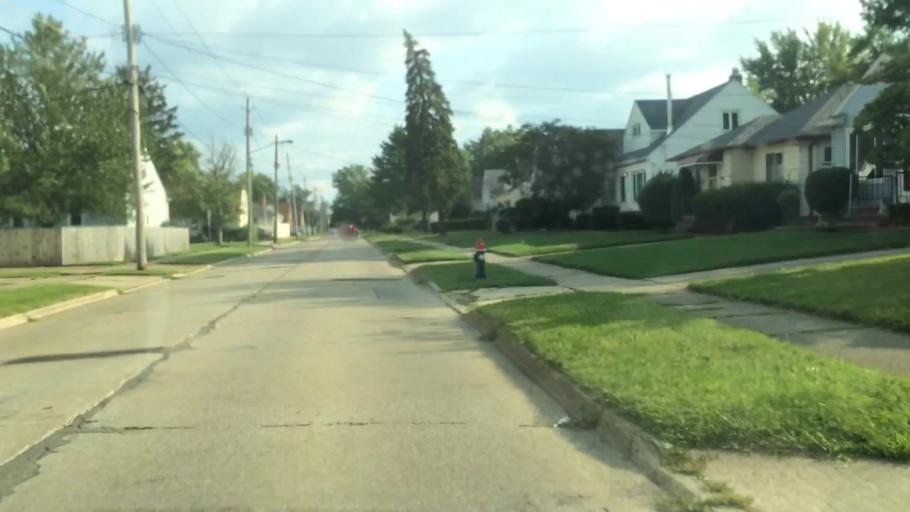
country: US
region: Ohio
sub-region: Cuyahoga County
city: Parma Heights
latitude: 41.3961
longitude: -81.7449
